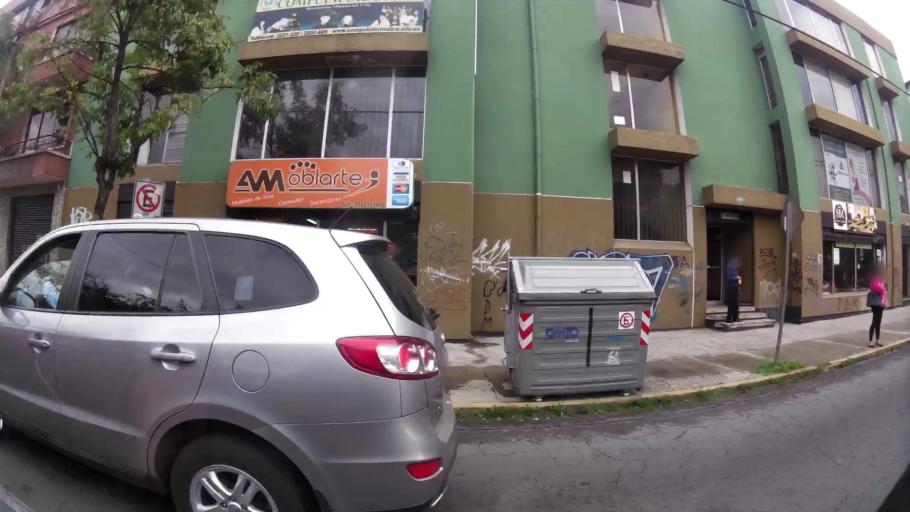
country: EC
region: Pichincha
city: Quito
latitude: -0.1951
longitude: -78.4992
